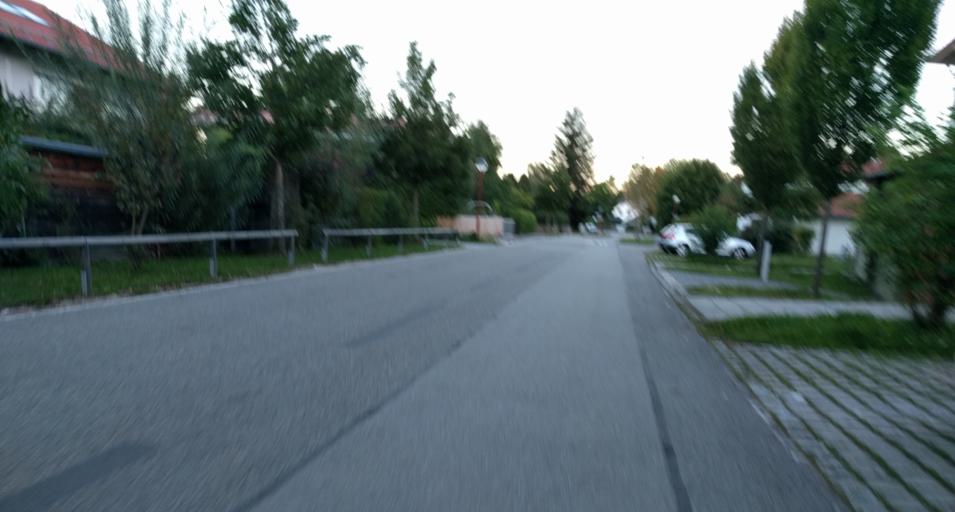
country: DE
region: Bavaria
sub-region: Upper Bavaria
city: Oberhaching
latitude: 48.0244
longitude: 11.5718
